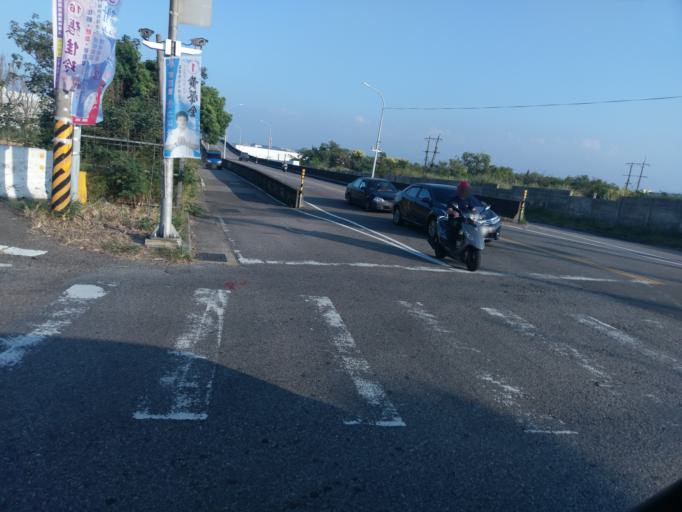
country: TW
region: Taiwan
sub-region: Miaoli
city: Miaoli
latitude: 24.6767
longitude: 120.8771
